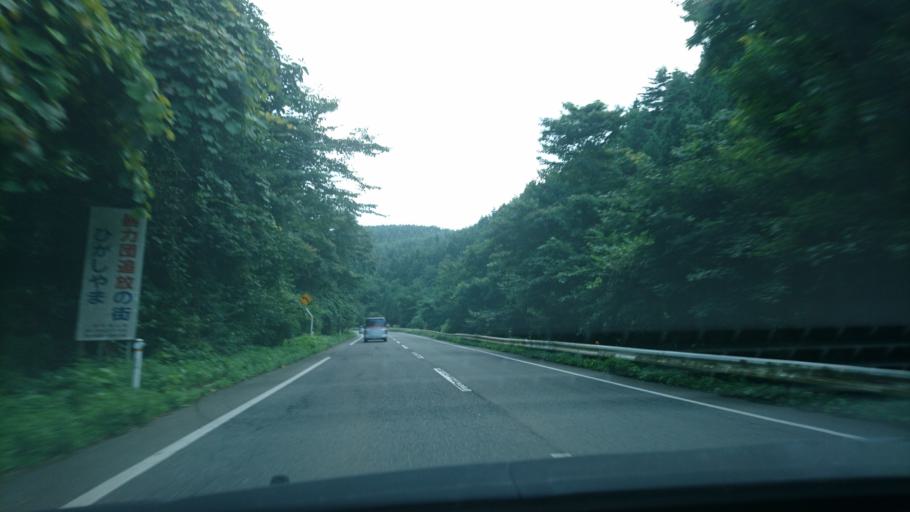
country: JP
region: Iwate
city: Mizusawa
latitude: 39.0566
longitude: 141.2269
